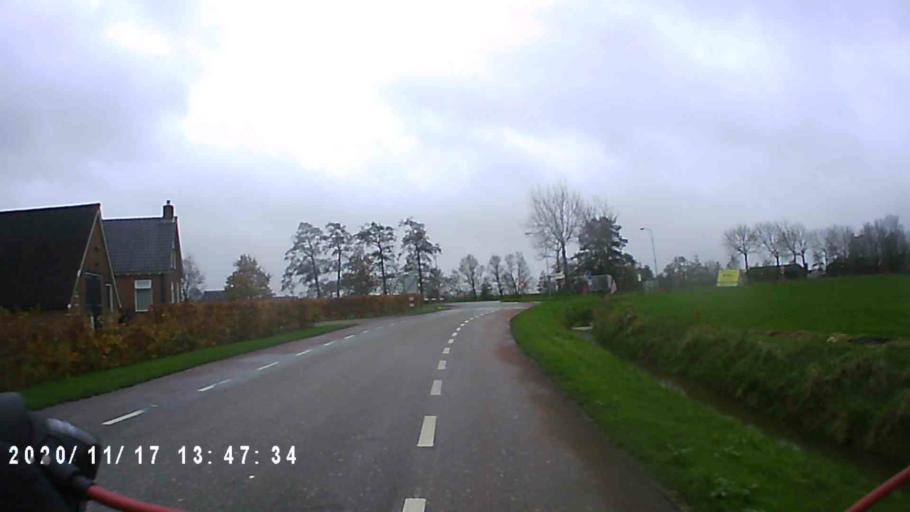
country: NL
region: Groningen
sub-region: Gemeente Zuidhorn
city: Zuidhorn
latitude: 53.2332
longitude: 6.3747
